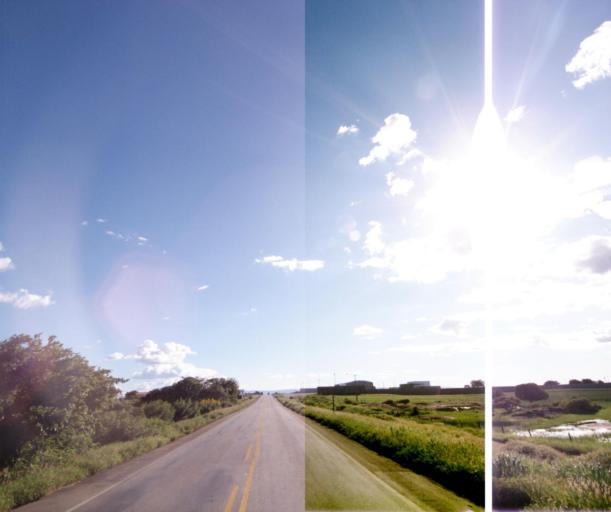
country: BR
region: Bahia
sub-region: Guanambi
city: Guanambi
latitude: -14.1750
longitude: -42.7293
